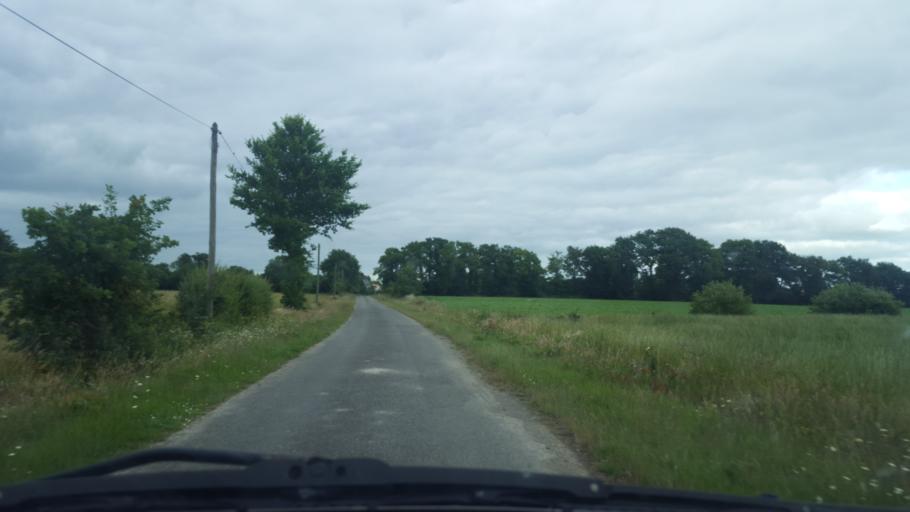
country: FR
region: Pays de la Loire
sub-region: Departement de la Loire-Atlantique
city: Saint-Philbert-de-Grand-Lieu
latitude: 47.0135
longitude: -1.6807
